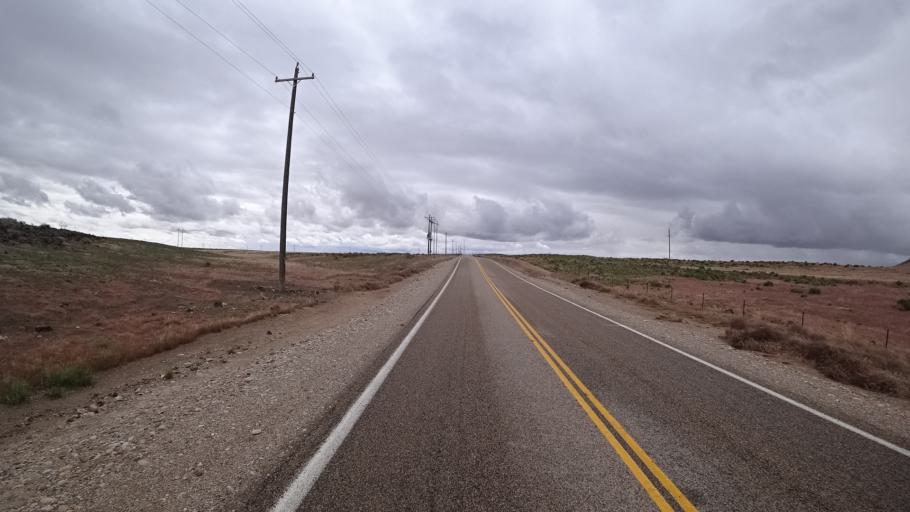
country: US
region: Idaho
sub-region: Owyhee County
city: Murphy
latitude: 43.2441
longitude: -116.3694
